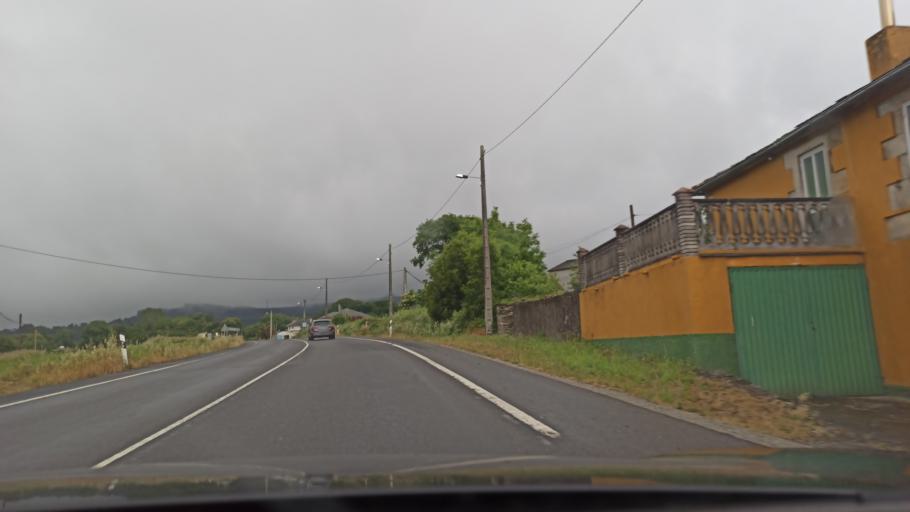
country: ES
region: Galicia
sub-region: Provincia de Lugo
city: Ourol
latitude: 42.9462
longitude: -7.6248
